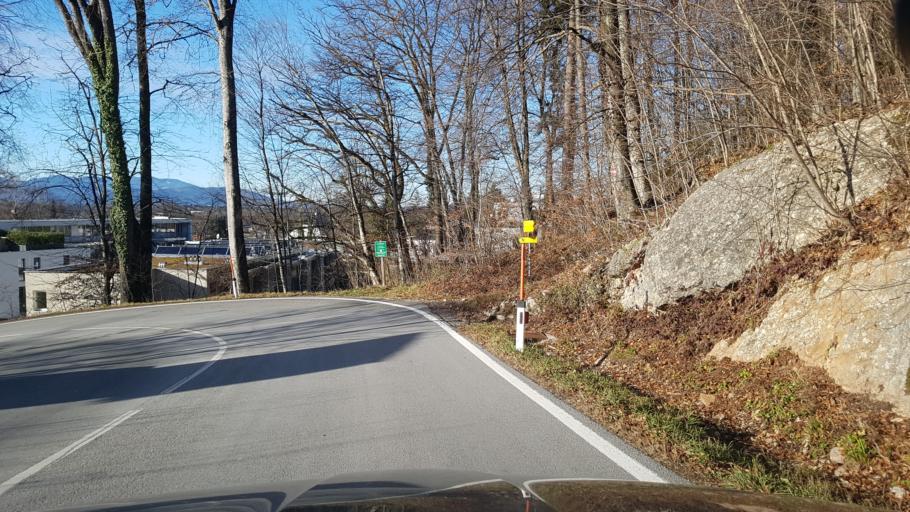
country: AT
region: Salzburg
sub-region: Politischer Bezirk Salzburg-Umgebung
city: Elsbethen
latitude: 47.7703
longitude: 13.0894
